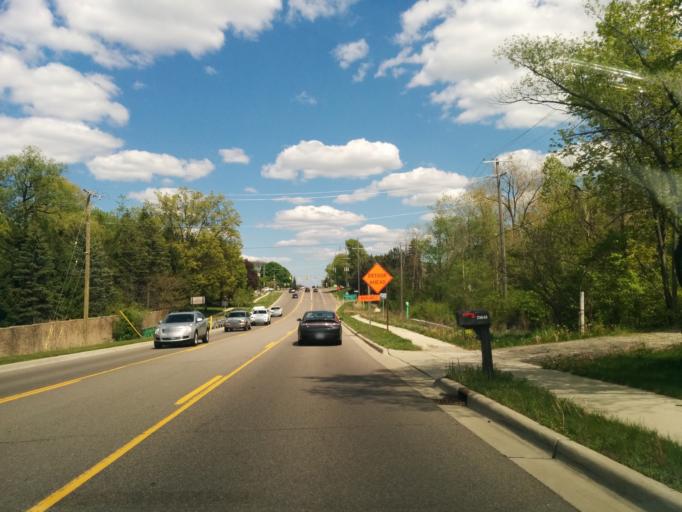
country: US
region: Michigan
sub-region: Oakland County
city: Franklin
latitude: 42.5142
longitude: -83.3432
